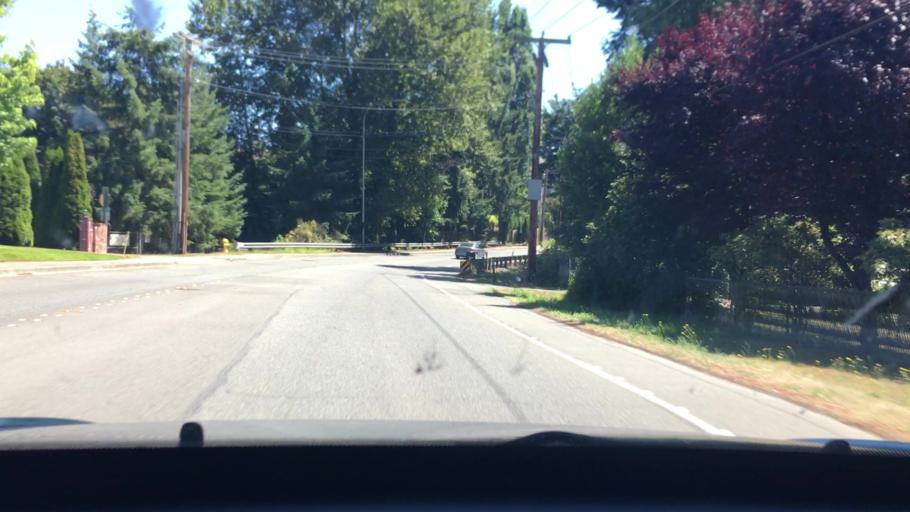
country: US
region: Washington
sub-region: King County
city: Newcastle
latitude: 47.5065
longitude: -122.1528
